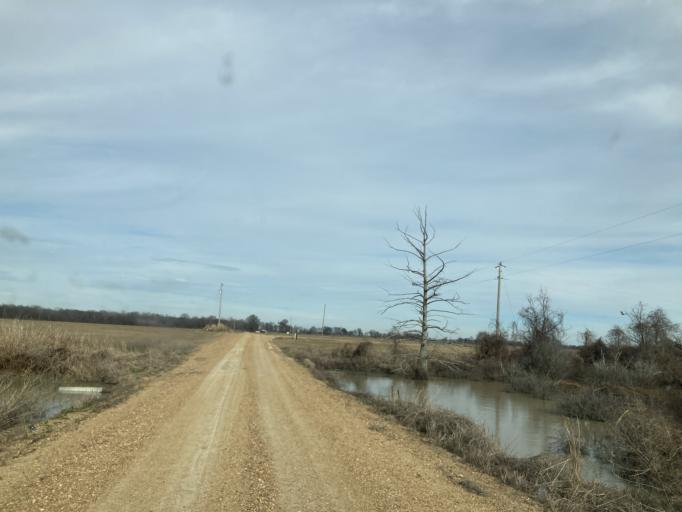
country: US
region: Mississippi
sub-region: Humphreys County
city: Belzoni
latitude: 33.0591
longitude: -90.6577
